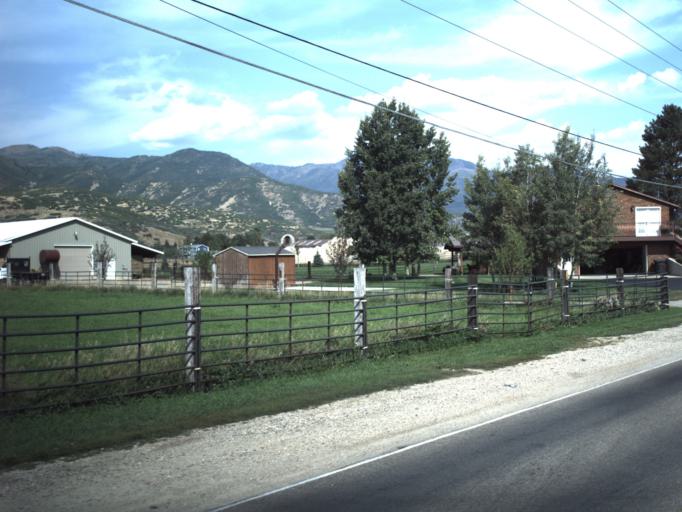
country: US
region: Utah
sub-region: Wasatch County
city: Midway
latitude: 40.4984
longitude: -111.4720
